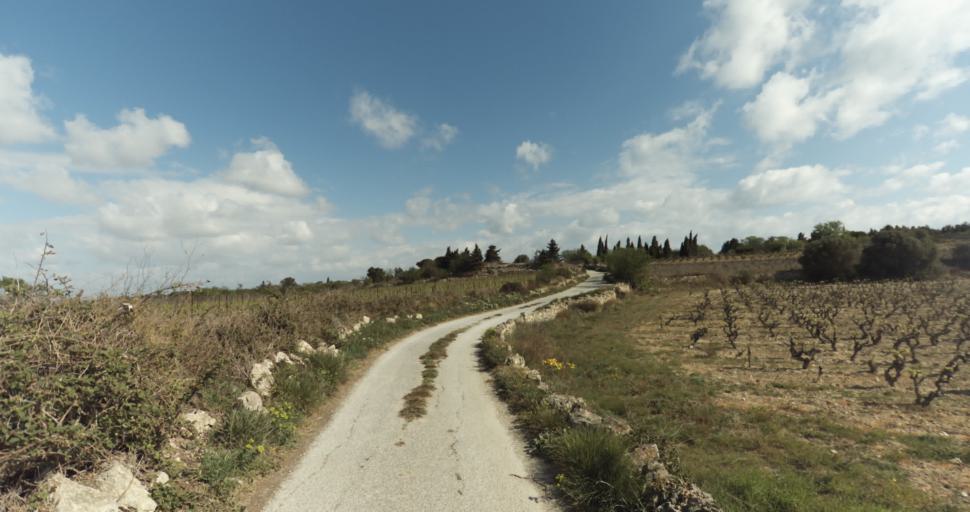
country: FR
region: Languedoc-Roussillon
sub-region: Departement de l'Aude
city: Leucate
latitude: 42.9235
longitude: 3.0365
